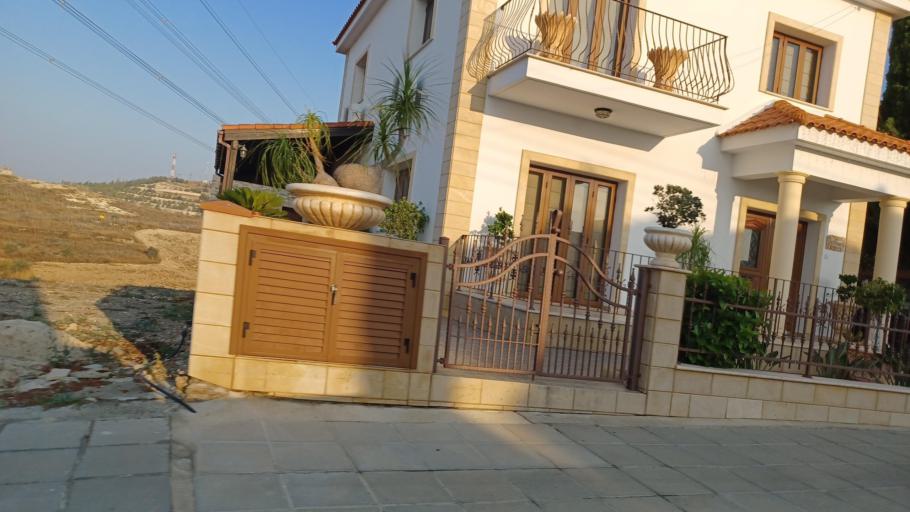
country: CY
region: Larnaka
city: Pyla
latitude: 35.0047
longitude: 33.6845
